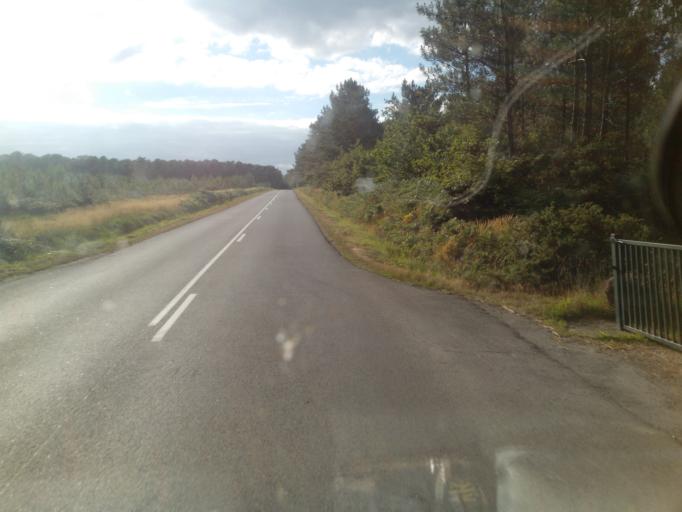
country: FR
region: Brittany
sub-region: Departement d'Ille-et-Vilaine
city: Plelan-le-Grand
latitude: 48.0073
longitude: -2.1218
